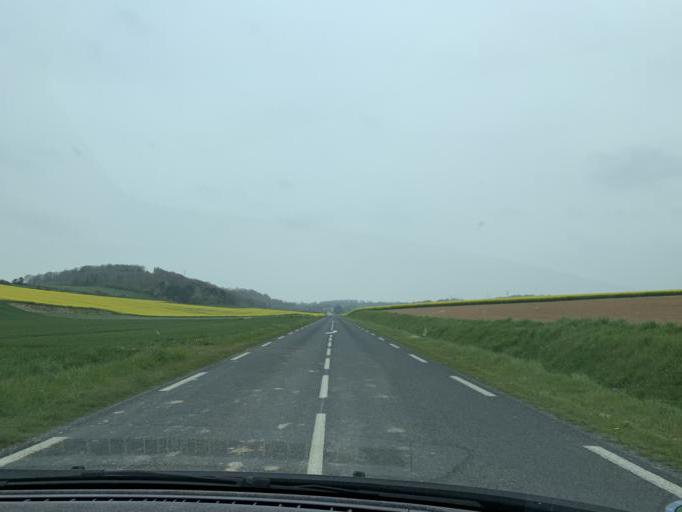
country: FR
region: Haute-Normandie
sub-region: Departement de la Seine-Maritime
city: Londinieres
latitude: 49.8425
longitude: 1.4217
